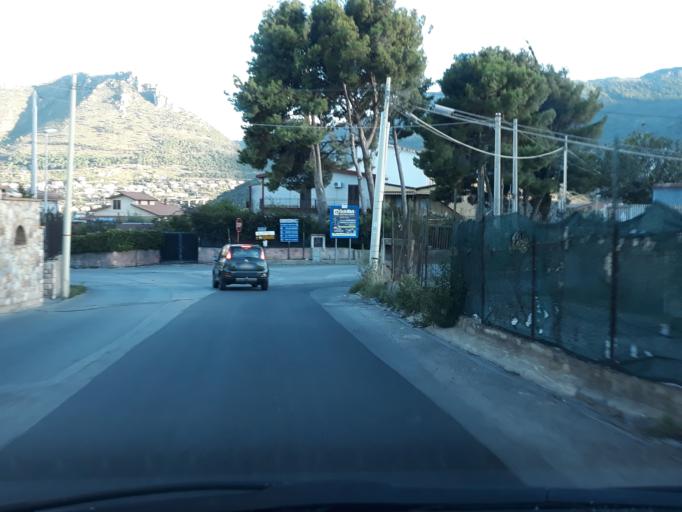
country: IT
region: Sicily
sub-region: Palermo
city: Monreale
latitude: 38.0718
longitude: 13.2967
